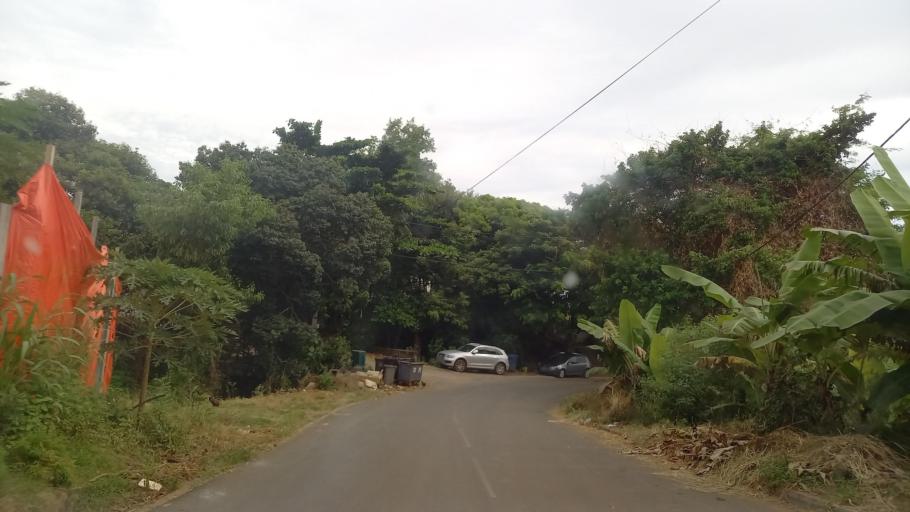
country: YT
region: Boueni
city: Boueni
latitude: -12.9059
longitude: 45.0828
